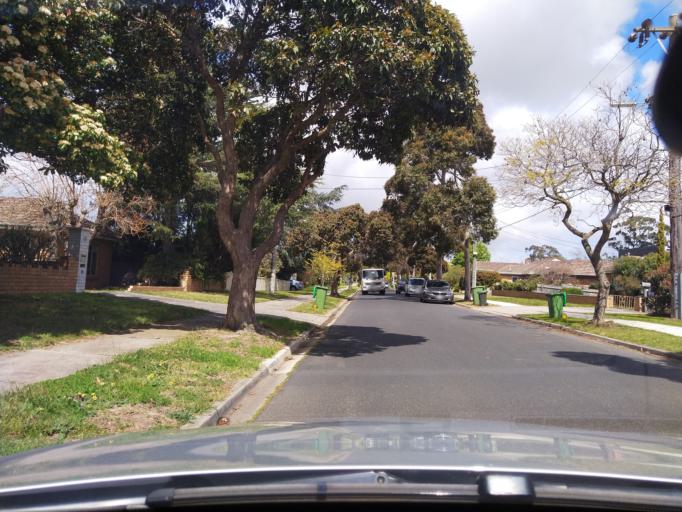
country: AU
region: Victoria
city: Rosanna
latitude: -37.7488
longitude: 145.0734
